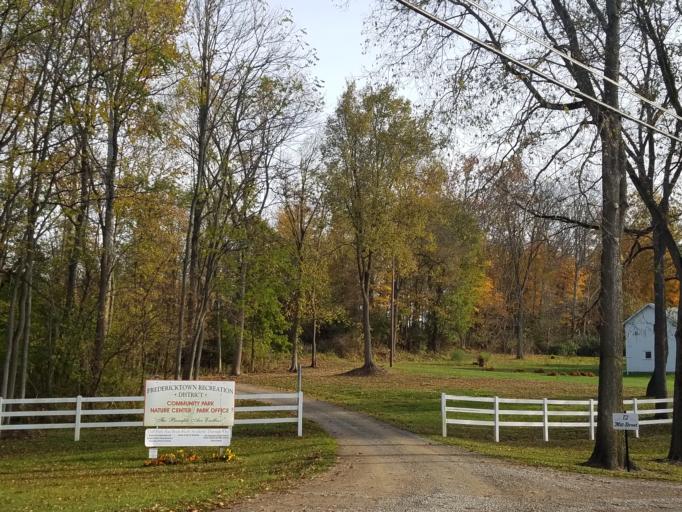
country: US
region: Ohio
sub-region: Knox County
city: Fredericktown
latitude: 40.4848
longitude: -82.5413
